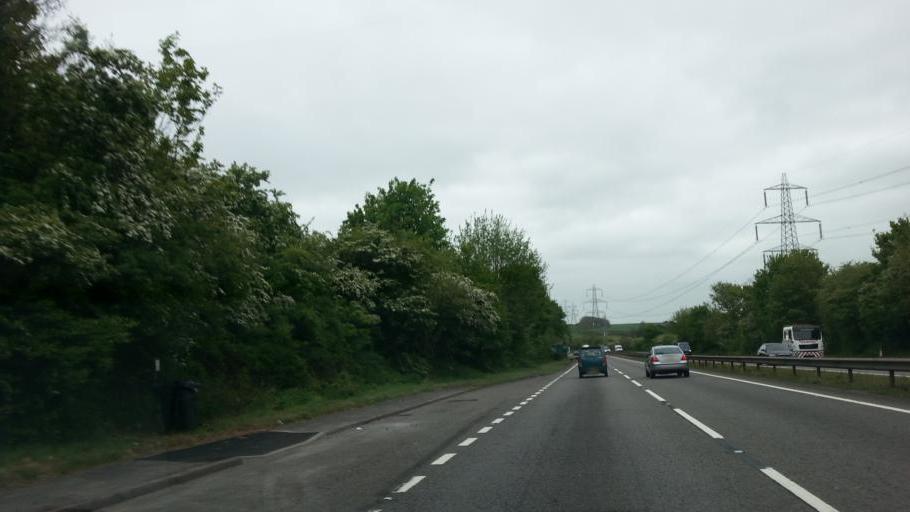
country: GB
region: England
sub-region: Lincolnshire
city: Barrowby
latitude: 52.9030
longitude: -0.6706
